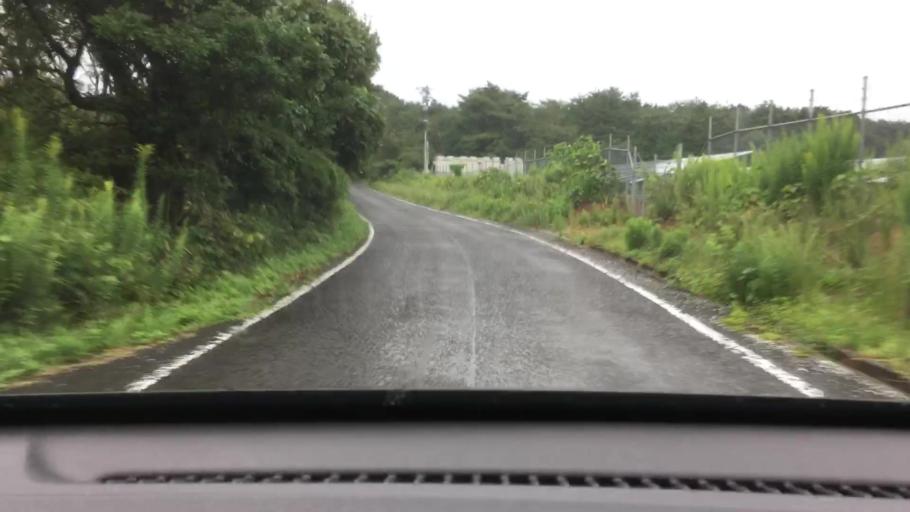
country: JP
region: Nagasaki
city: Togitsu
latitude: 32.9230
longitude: 129.7236
